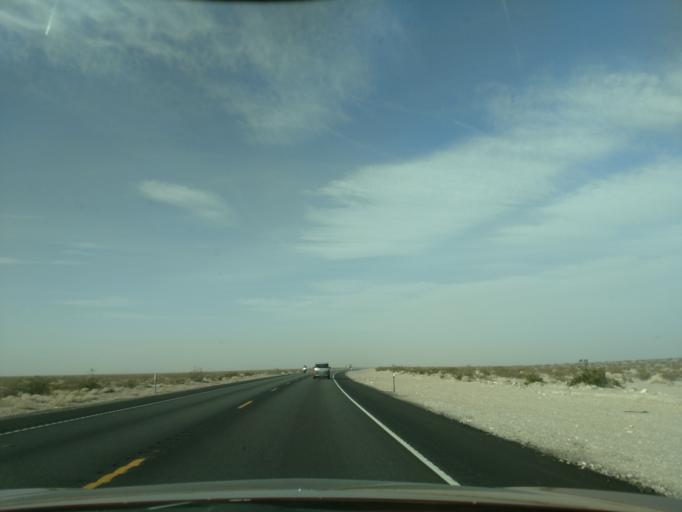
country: US
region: Nevada
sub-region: Nye County
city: Beatty
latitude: 36.6319
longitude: -116.3514
